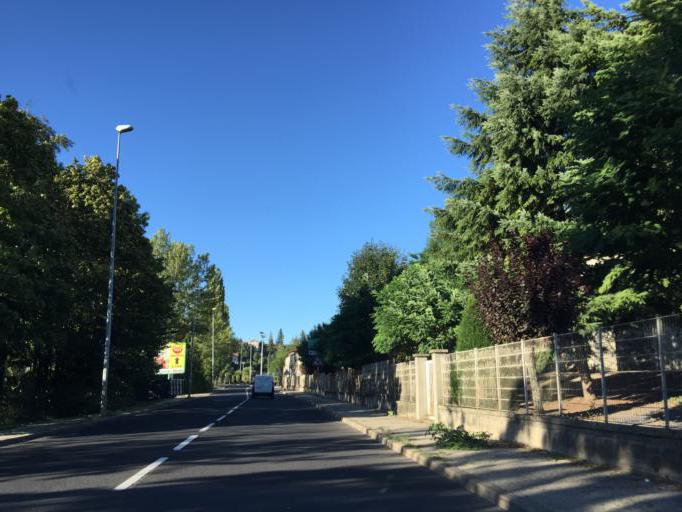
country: FR
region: Auvergne
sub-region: Departement de la Haute-Loire
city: Chadrac
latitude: 45.0539
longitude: 3.9014
